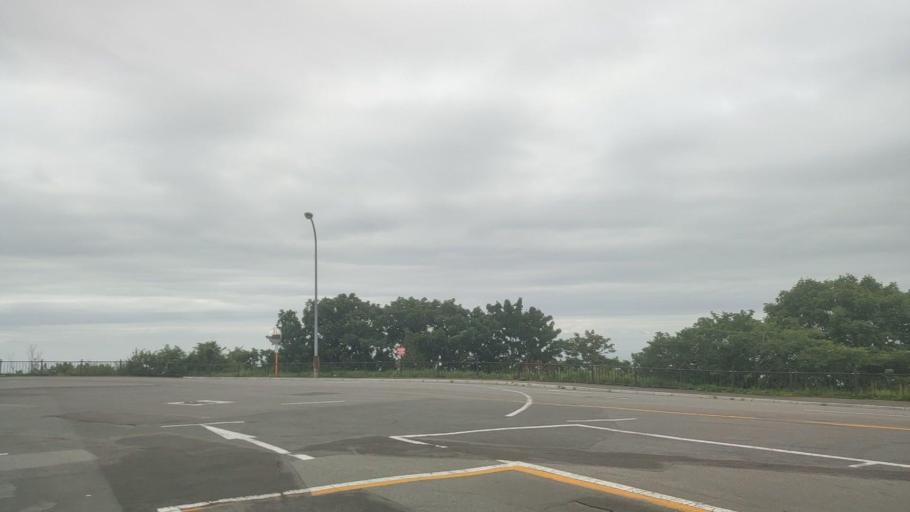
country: JP
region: Hokkaido
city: Hakodate
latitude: 41.7590
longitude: 140.7036
